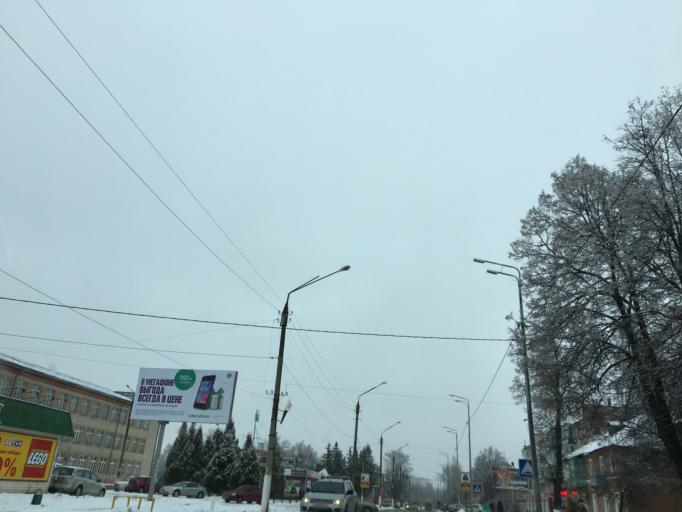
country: RU
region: Tula
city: Donskoy
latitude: 53.9674
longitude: 38.3181
